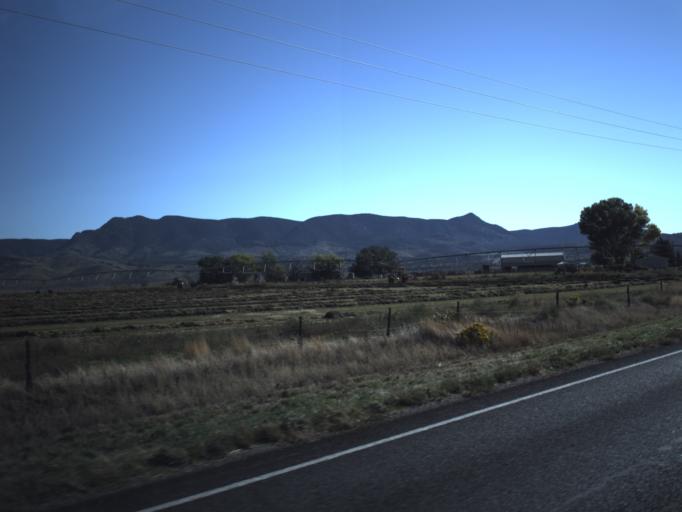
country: US
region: Utah
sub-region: Washington County
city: Enterprise
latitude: 37.6738
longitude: -113.5572
